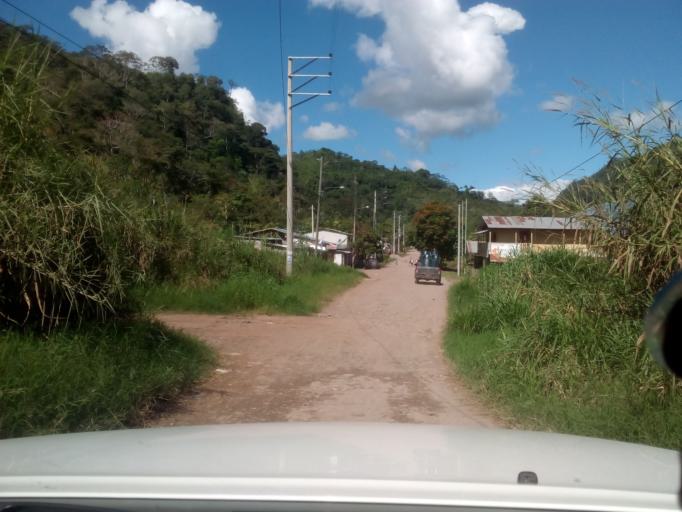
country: PE
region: Pasco
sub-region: Provincia de Oxapampa
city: Villa Rica
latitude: -10.8380
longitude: -75.2898
